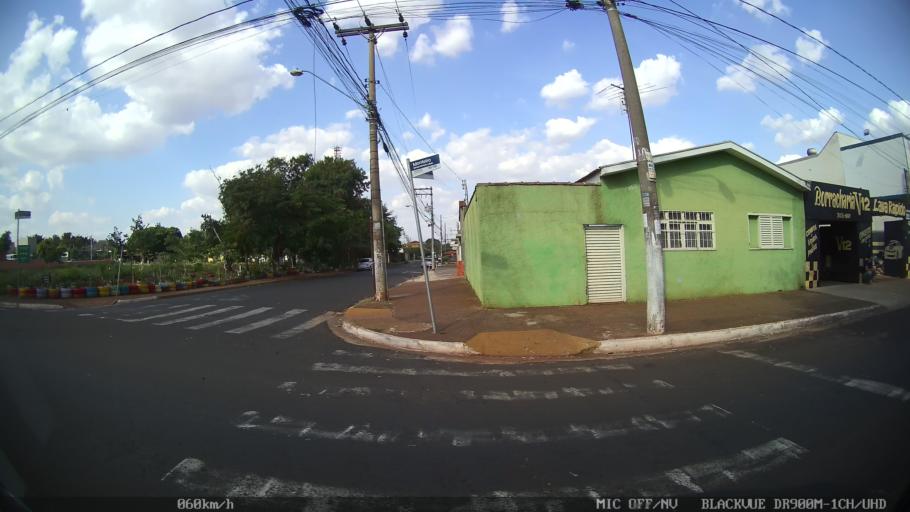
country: BR
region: Sao Paulo
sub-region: Ribeirao Preto
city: Ribeirao Preto
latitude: -21.1919
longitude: -47.8375
